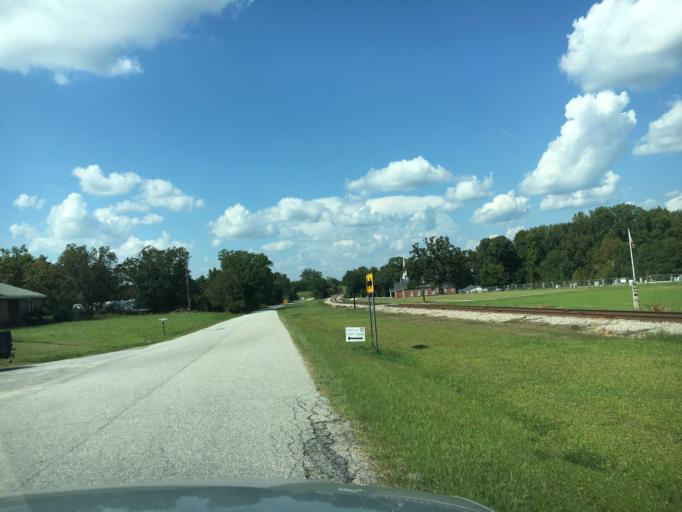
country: US
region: South Carolina
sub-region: Laurens County
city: Laurens
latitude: 34.5838
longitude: -82.1024
